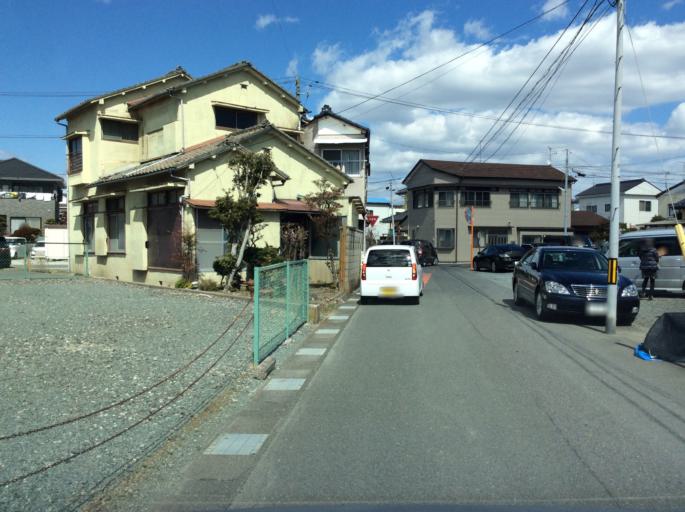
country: JP
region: Fukushima
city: Iwaki
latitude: 36.9532
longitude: 140.9059
